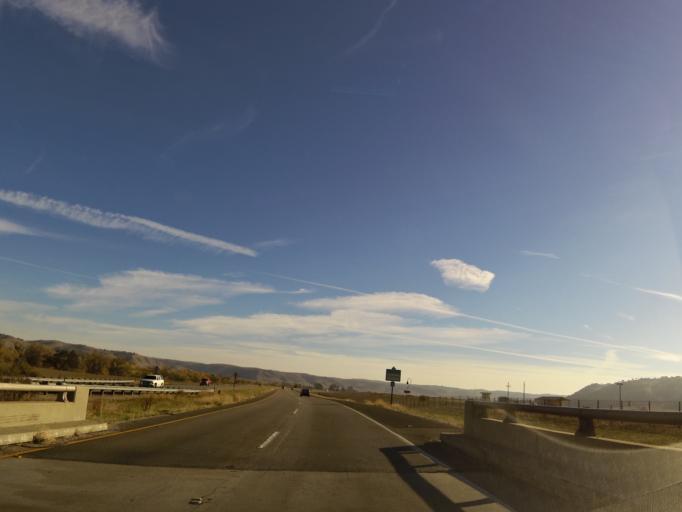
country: US
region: California
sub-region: San Luis Obispo County
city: San Miguel
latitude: 35.8550
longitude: -120.7996
